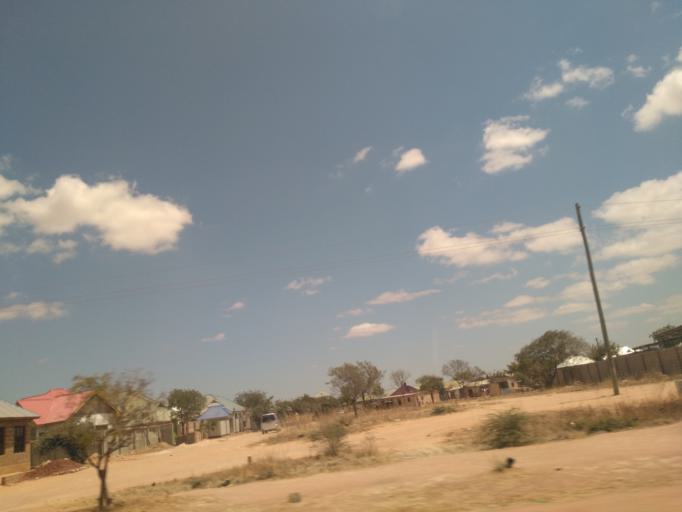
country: TZ
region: Dodoma
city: Kisasa
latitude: -6.1622
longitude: 35.7912
